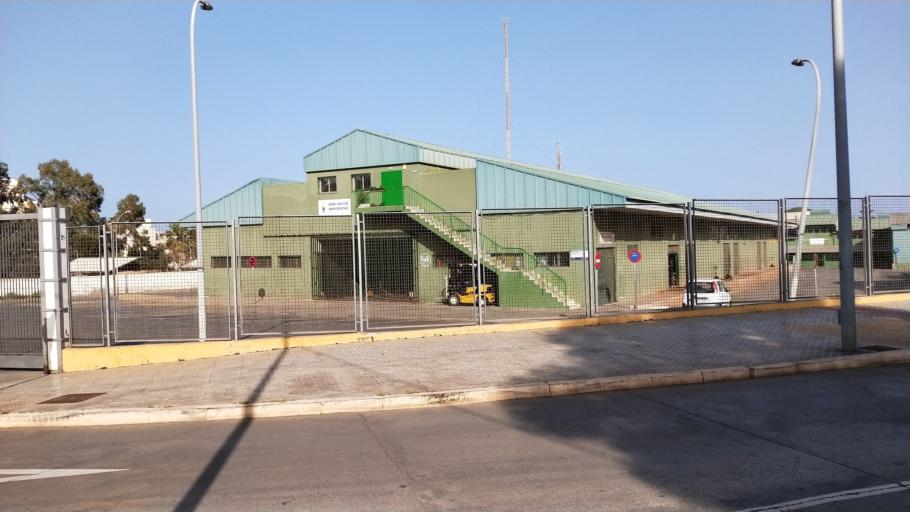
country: ES
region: Melilla
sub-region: Melilla
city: Melilla
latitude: 35.2798
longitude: -2.9506
